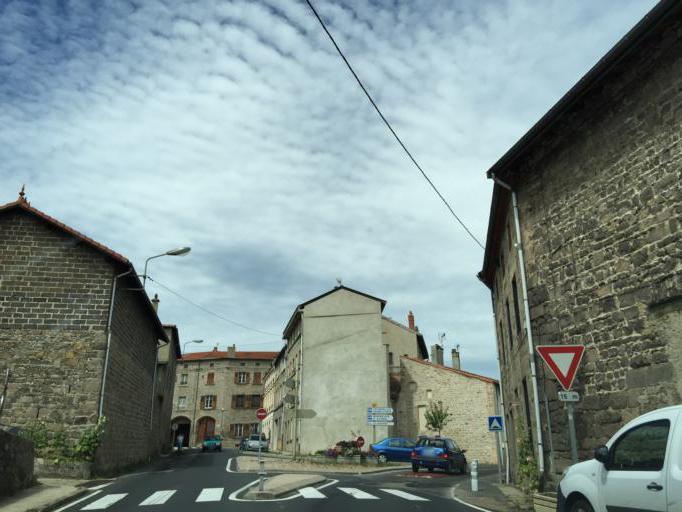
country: FR
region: Rhone-Alpes
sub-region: Departement de la Loire
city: Saint-Bonnet-le-Chateau
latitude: 45.4251
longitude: 4.0674
